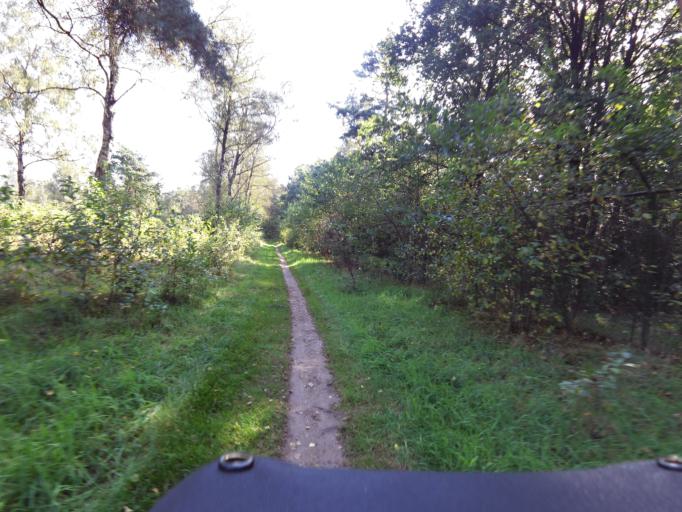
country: NL
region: Gelderland
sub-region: Gemeente Apeldoorn
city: Uddel
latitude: 52.2261
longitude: 5.7700
